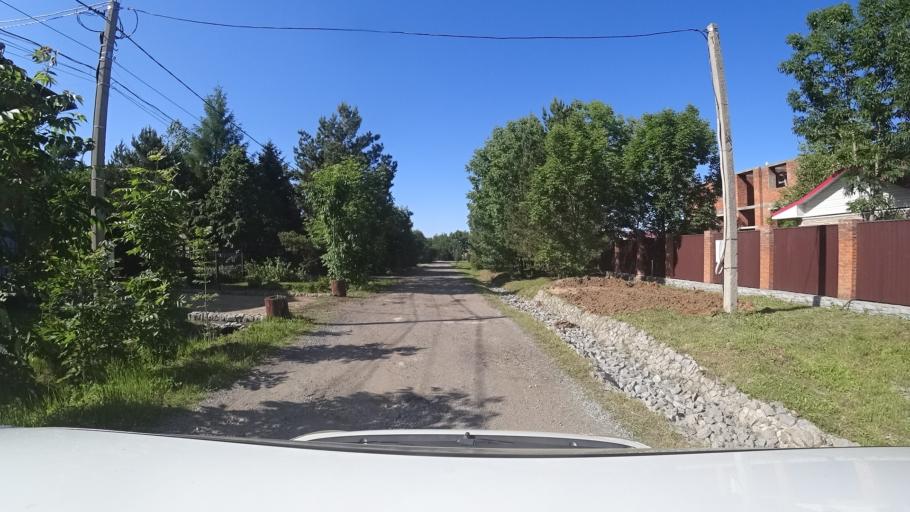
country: RU
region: Khabarovsk Krai
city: Topolevo
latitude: 48.5474
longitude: 135.1797
